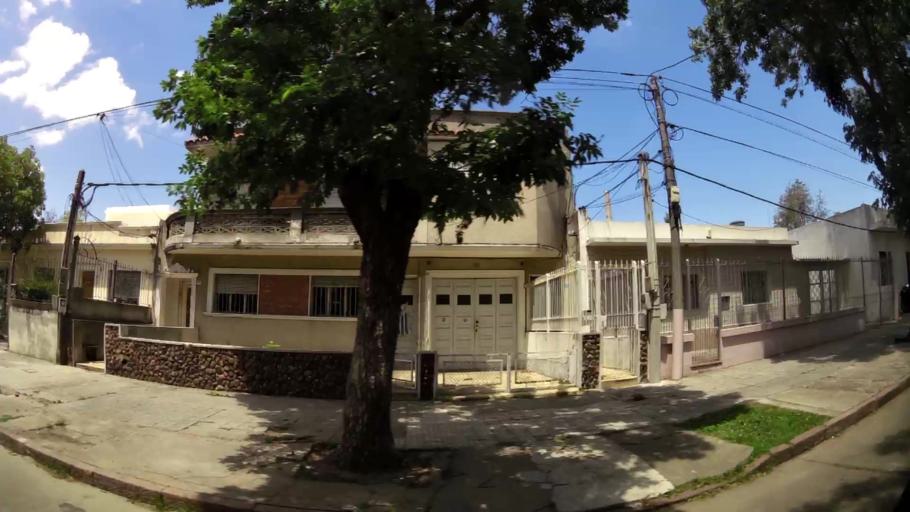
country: UY
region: Montevideo
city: Montevideo
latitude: -34.8651
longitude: -56.1888
